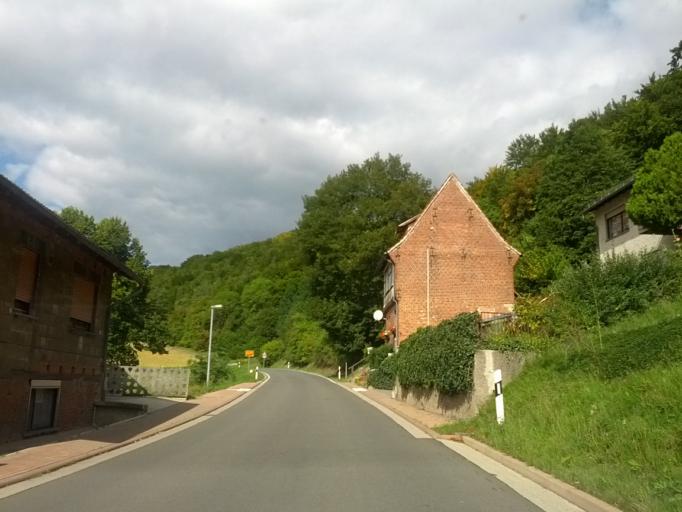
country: DE
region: Hesse
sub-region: Regierungsbezirk Kassel
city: Herleshausen
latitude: 51.0308
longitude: 10.1506
